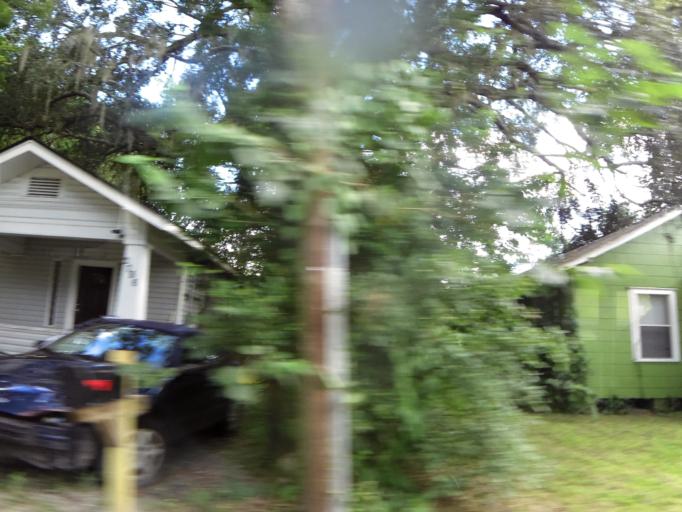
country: US
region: Florida
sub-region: Duval County
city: Jacksonville
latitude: 30.3247
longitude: -81.6982
